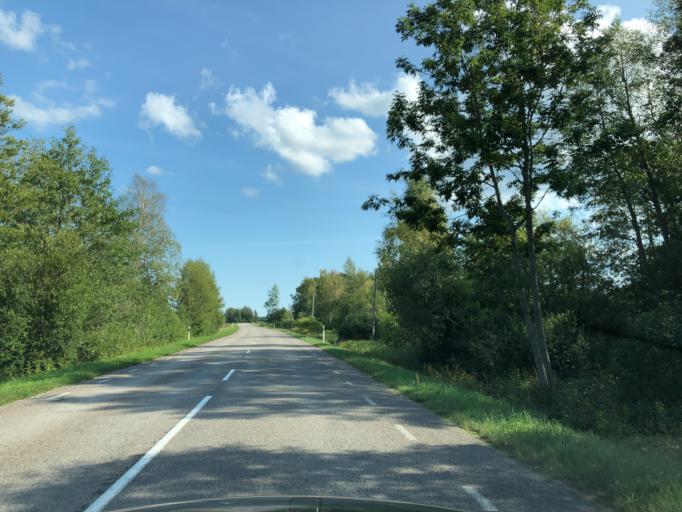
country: EE
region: Hiiumaa
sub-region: Kaerdla linn
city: Kardla
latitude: 58.7184
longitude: 22.5659
